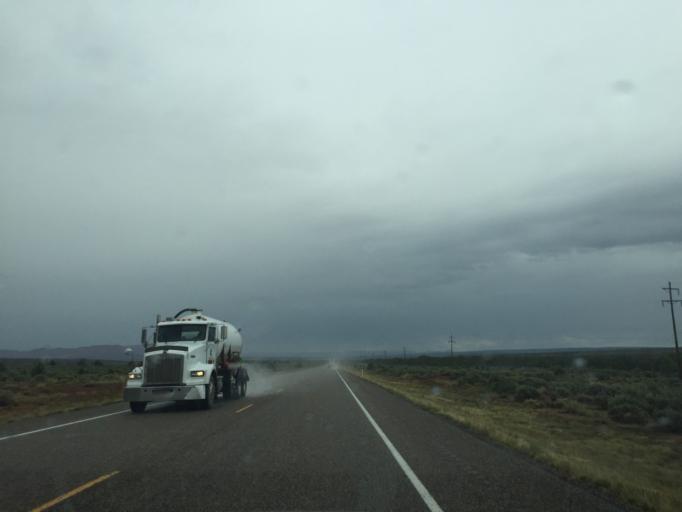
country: US
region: Utah
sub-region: Kane County
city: Kanab
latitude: 37.0820
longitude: -112.1589
